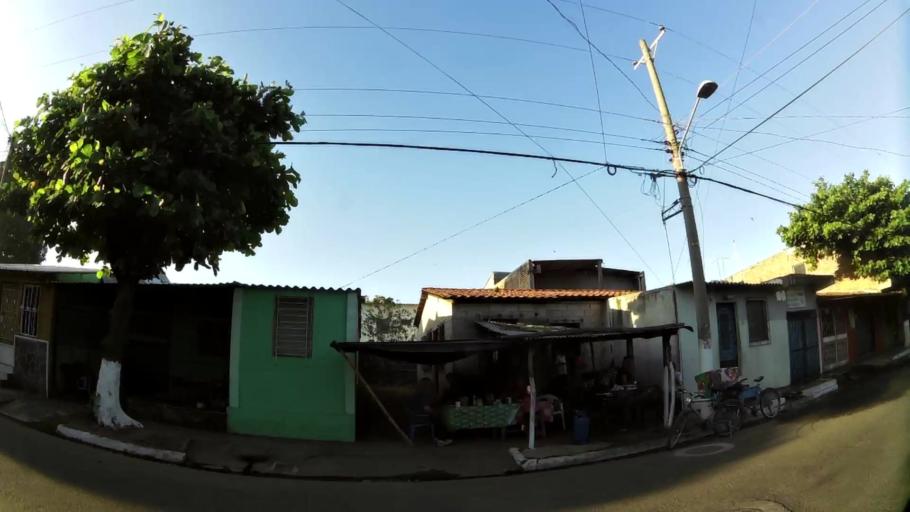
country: SV
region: Sonsonate
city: San Antonio del Monte
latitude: 13.7068
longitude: -89.7332
